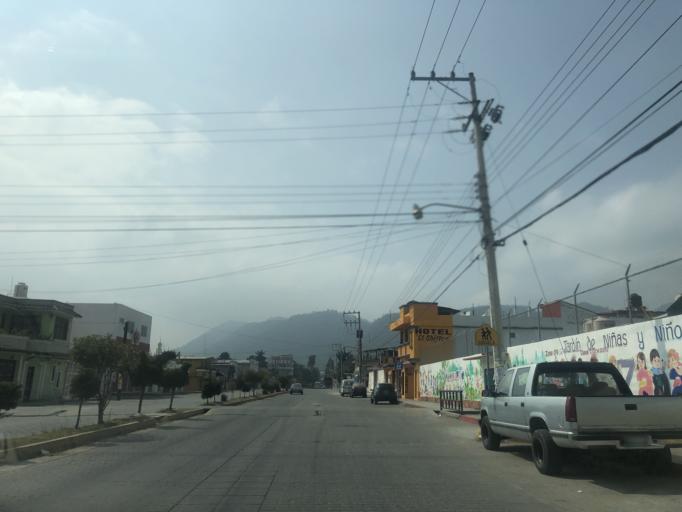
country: MX
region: Chiapas
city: San Cristobal de las Casas
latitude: 16.7158
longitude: -92.6358
